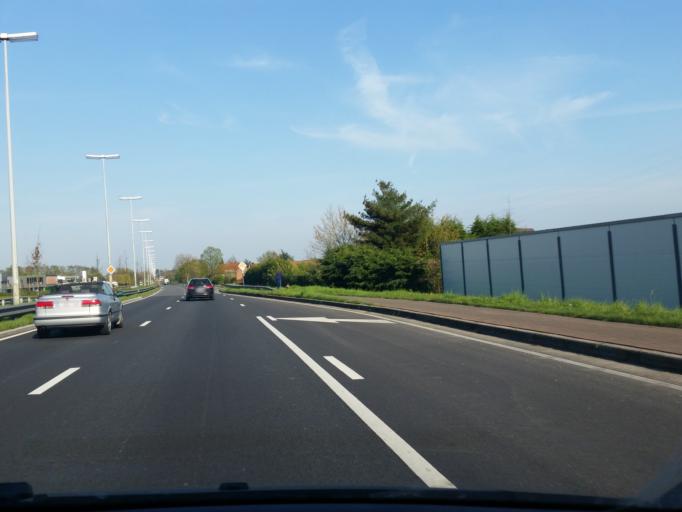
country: BE
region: Flanders
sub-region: Provincie Oost-Vlaanderen
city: Temse
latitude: 51.1344
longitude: 4.1923
